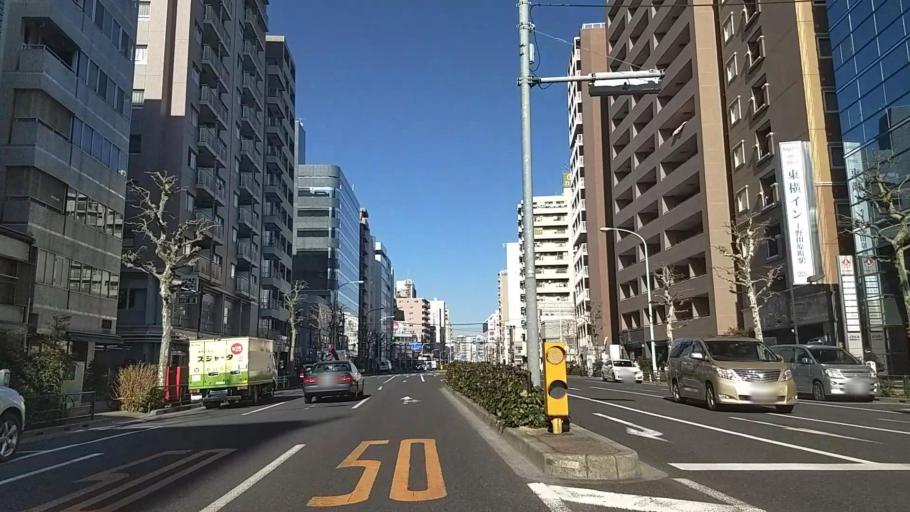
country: JP
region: Tokyo
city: Tokyo
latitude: 35.7076
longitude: 139.7909
